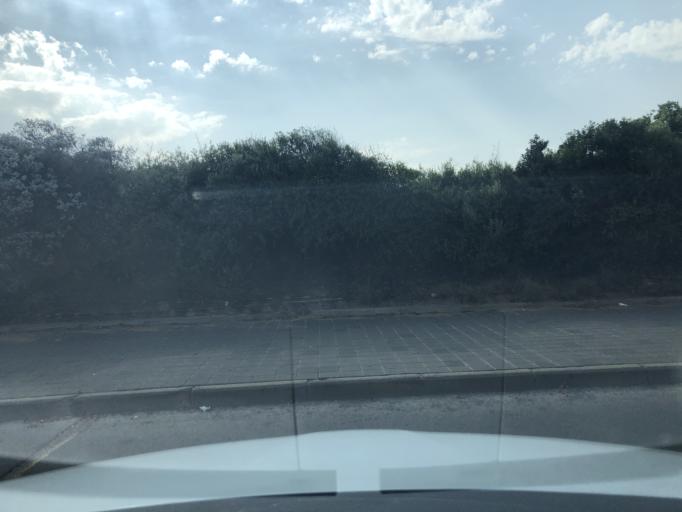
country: IL
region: Tel Aviv
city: Kefar Shemaryahu
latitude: 32.2150
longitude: 34.8167
